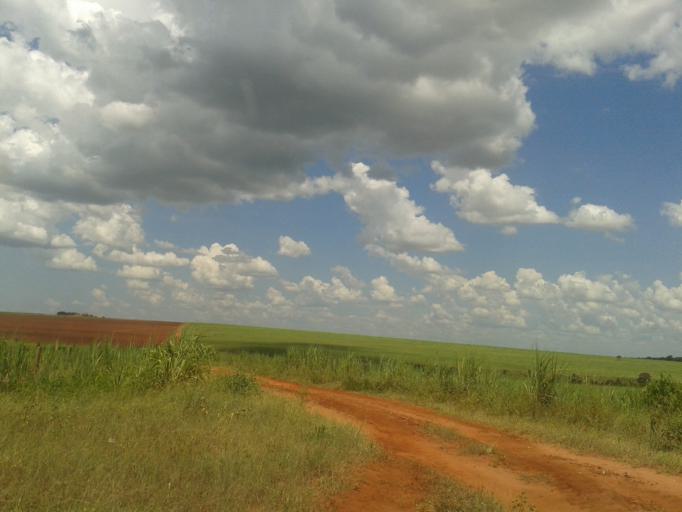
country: BR
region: Minas Gerais
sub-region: Santa Vitoria
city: Santa Vitoria
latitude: -19.1756
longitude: -50.4390
